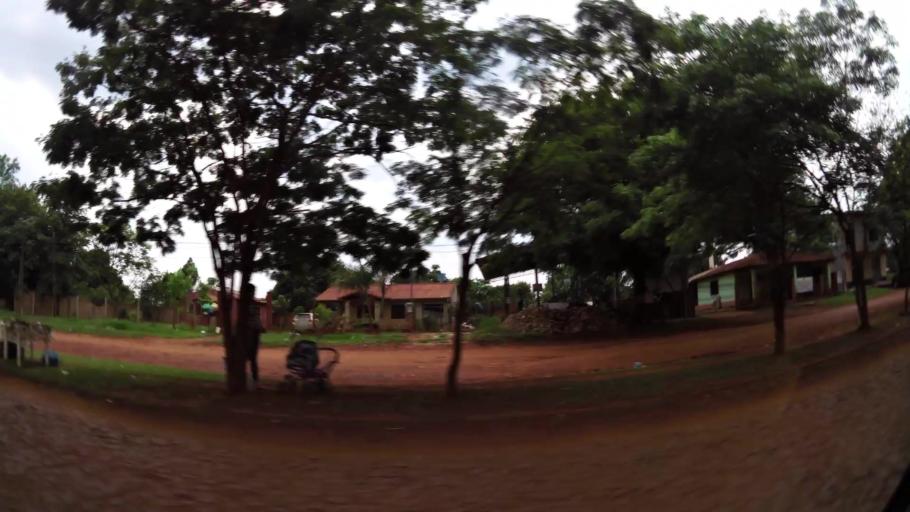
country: PY
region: Alto Parana
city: Presidente Franco
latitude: -25.5382
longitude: -54.6506
